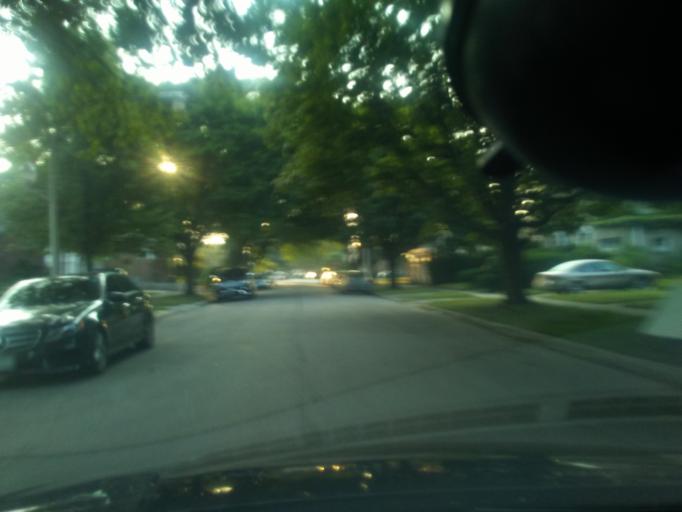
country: US
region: Illinois
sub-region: Cook County
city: Lincolnwood
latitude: 41.9804
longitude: -87.7002
